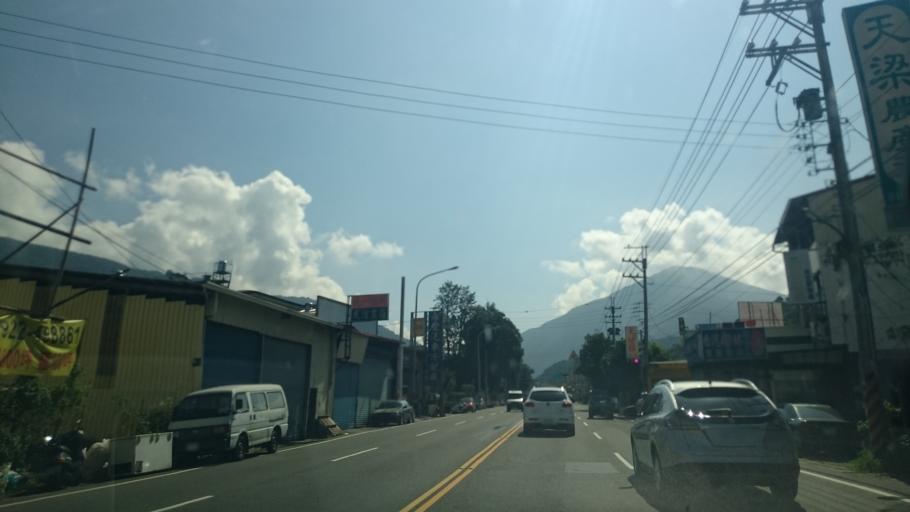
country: TW
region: Taiwan
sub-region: Nantou
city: Puli
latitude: 23.9757
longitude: 120.9831
